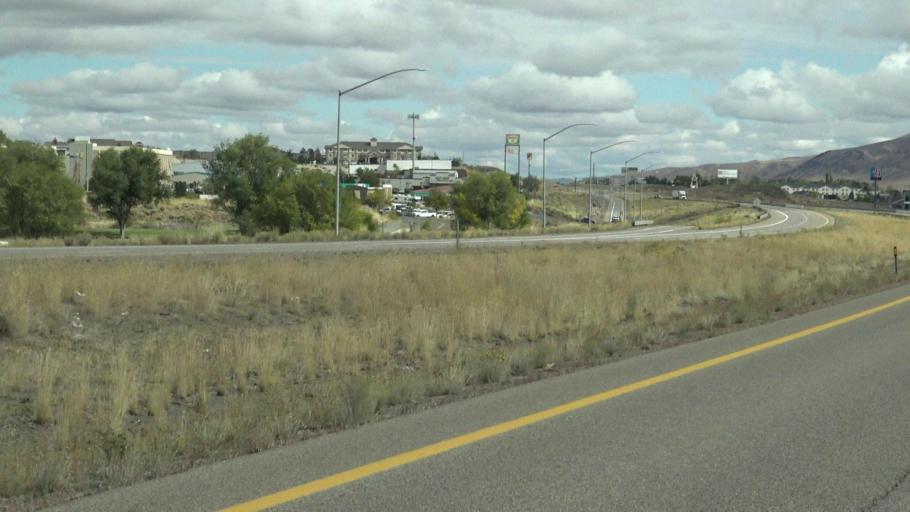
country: US
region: Nevada
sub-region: Elko County
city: Elko
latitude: 40.8493
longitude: -115.7527
